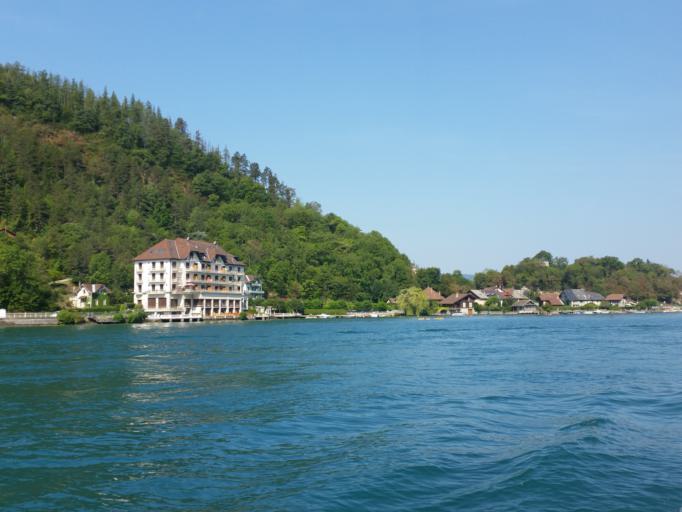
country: FR
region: Rhone-Alpes
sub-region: Departement de la Haute-Savoie
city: Talloires
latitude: 45.8258
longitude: 6.2107
